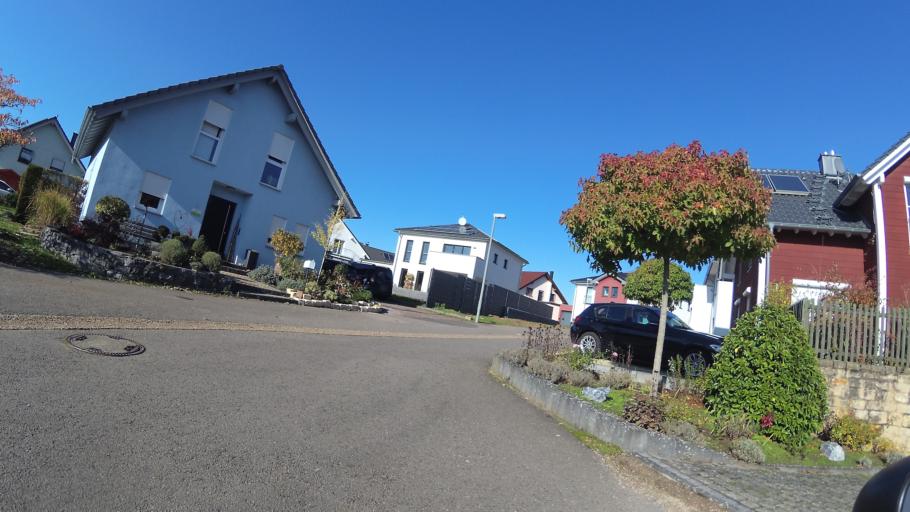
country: DE
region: Saarland
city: Britten
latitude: 49.4821
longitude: 6.7056
